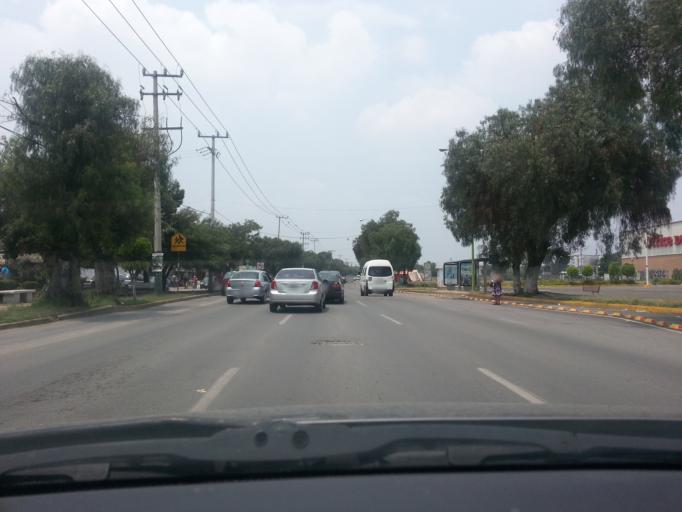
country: MX
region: Mexico
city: Cuautitlan Izcalli
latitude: 19.6641
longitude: -99.2112
